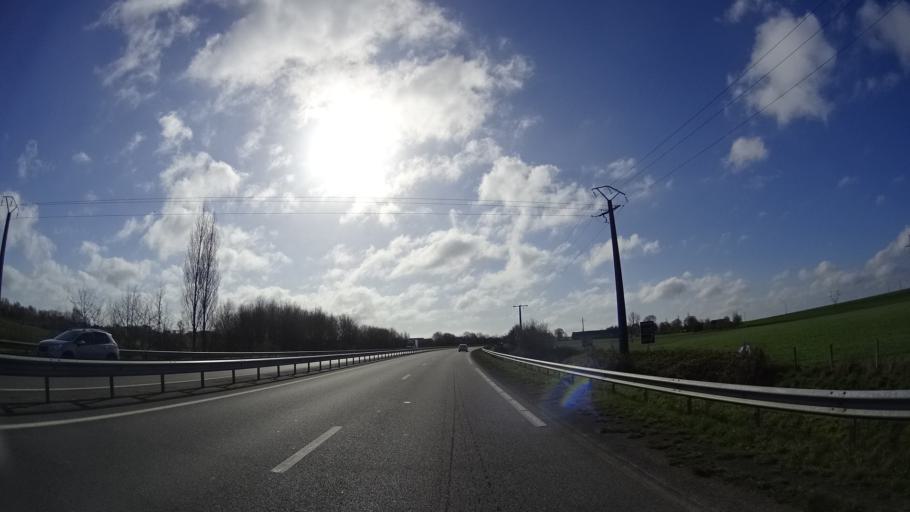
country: FR
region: Brittany
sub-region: Departement d'Ille-et-Vilaine
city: Janze
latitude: 47.9629
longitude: -1.5232
